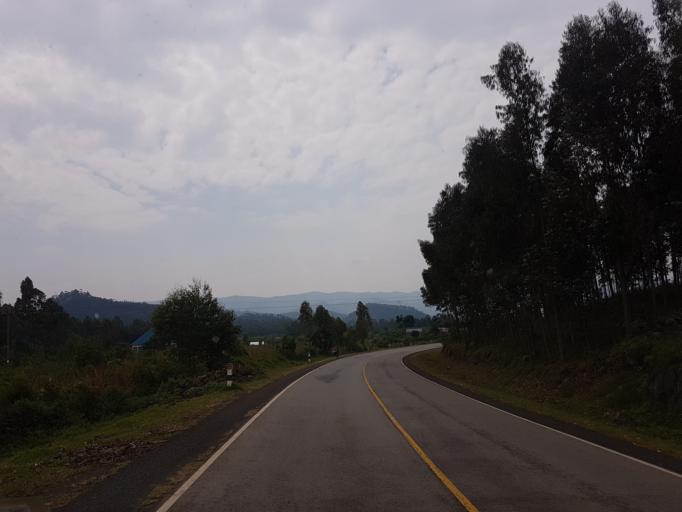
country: UG
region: Western Region
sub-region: Kisoro District
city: Kisoro
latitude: -1.3291
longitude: 29.7312
